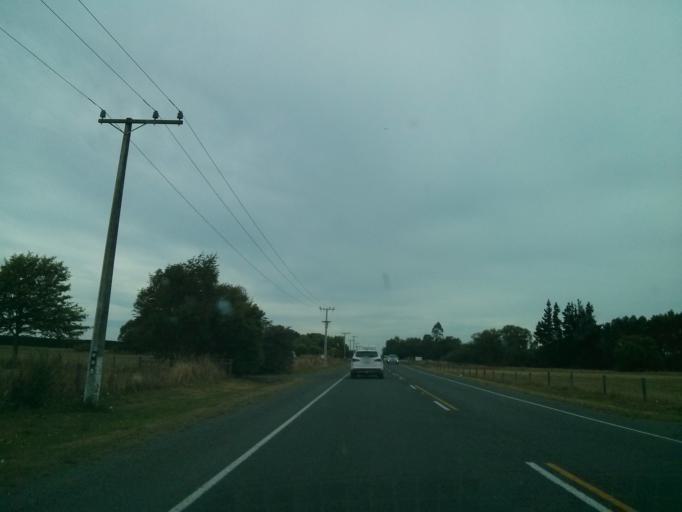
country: NZ
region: Canterbury
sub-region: Waimakariri District
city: Kaiapoi
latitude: -43.3990
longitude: 172.6080
